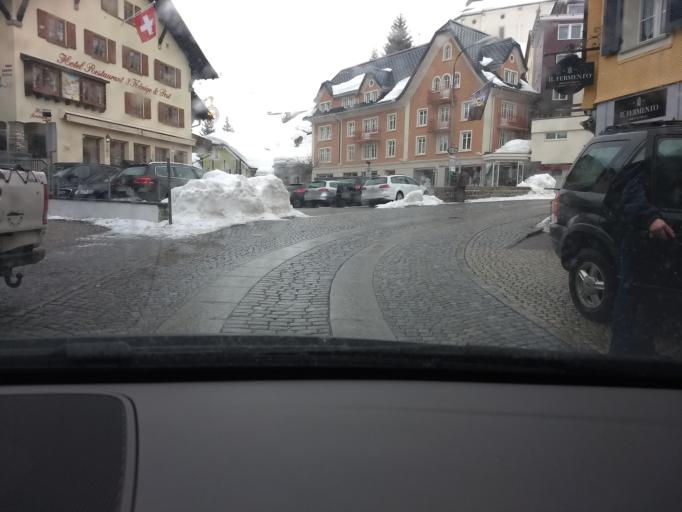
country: CH
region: Uri
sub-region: Uri
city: Andermatt
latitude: 46.6340
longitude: 8.5974
